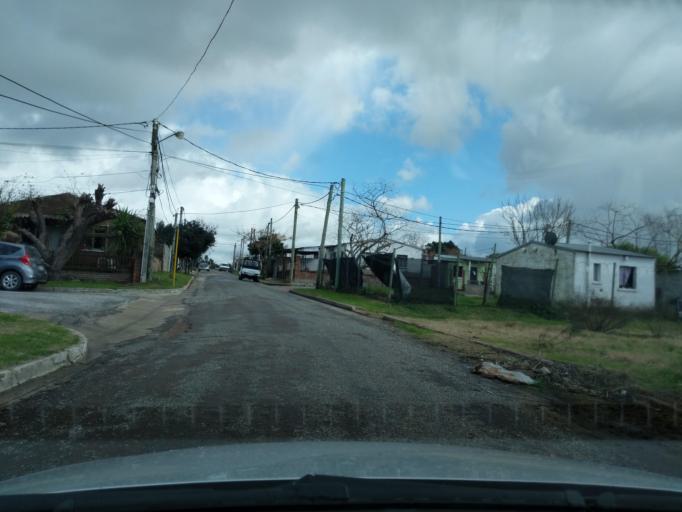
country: UY
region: Florida
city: Florida
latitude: -34.1032
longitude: -56.2251
